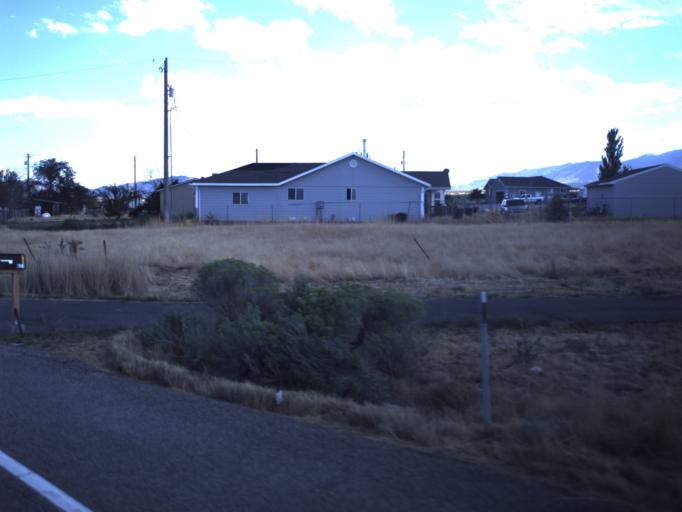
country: US
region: Utah
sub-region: Tooele County
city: Grantsville
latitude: 40.6164
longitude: -112.4989
